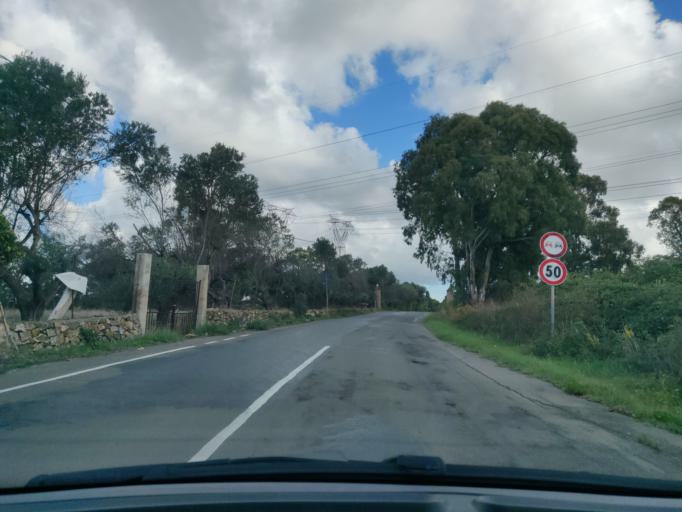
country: IT
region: Latium
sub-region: Citta metropolitana di Roma Capitale
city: Aurelia
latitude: 42.1309
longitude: 11.7878
